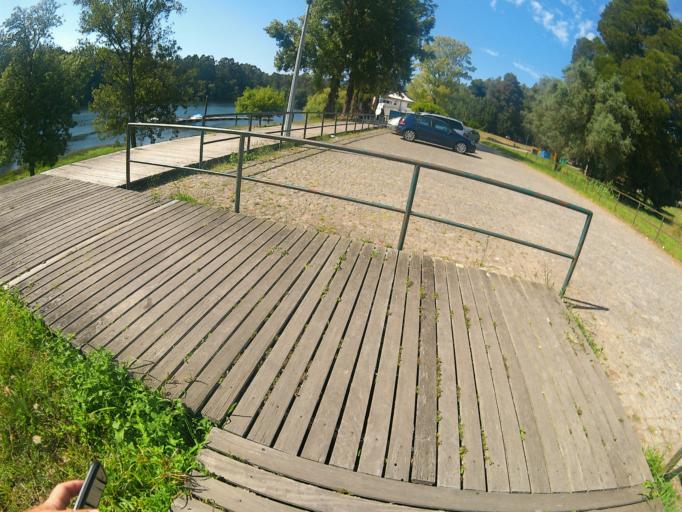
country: PT
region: Viana do Castelo
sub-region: Valenca
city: Valenca
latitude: 42.0231
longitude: -8.6569
